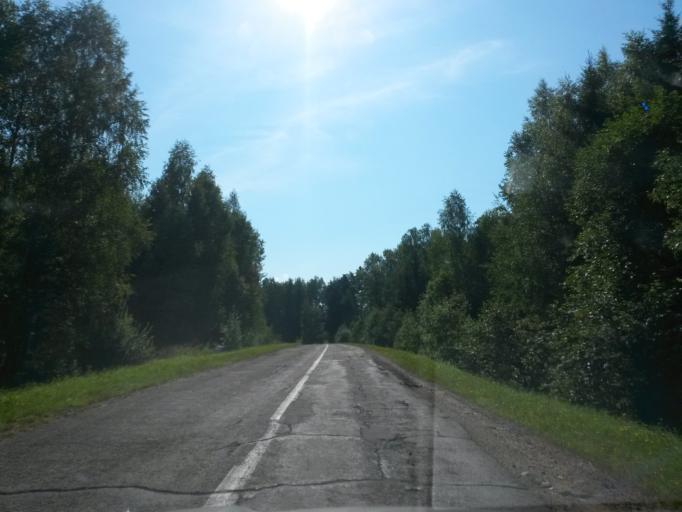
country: RU
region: Jaroslavl
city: Dubki
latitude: 57.2920
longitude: 40.0964
